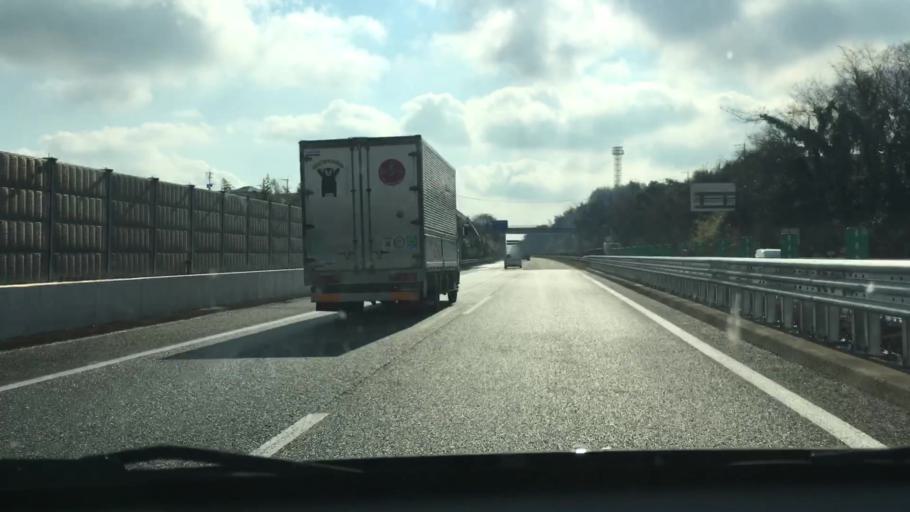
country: JP
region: Kumamoto
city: Kumamoto
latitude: 32.7305
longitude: 130.7749
